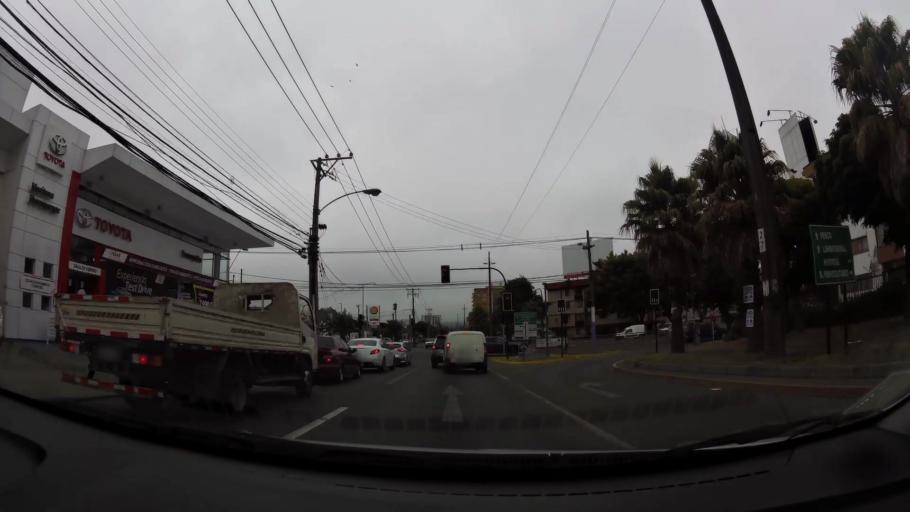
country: CL
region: Biobio
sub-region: Provincia de Concepcion
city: Concepcion
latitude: -36.8172
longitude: -73.0466
